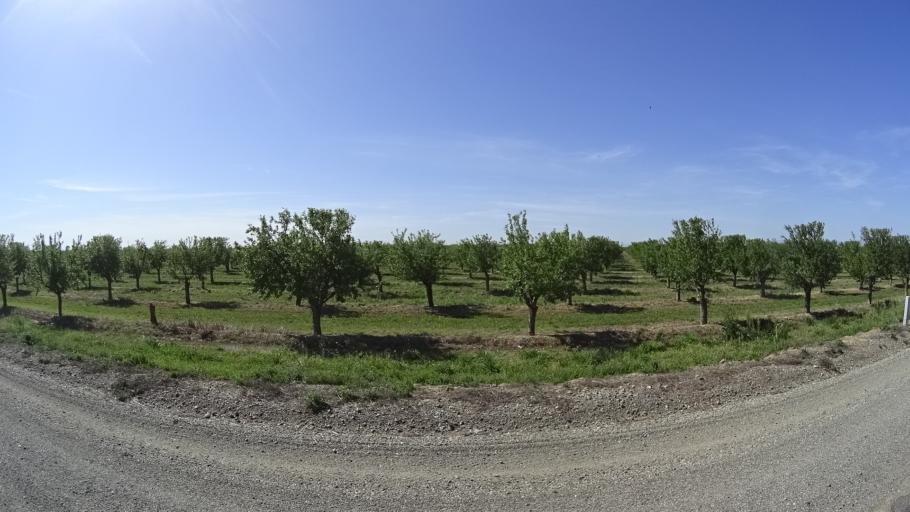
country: US
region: California
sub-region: Glenn County
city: Willows
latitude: 39.6239
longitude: -122.1634
